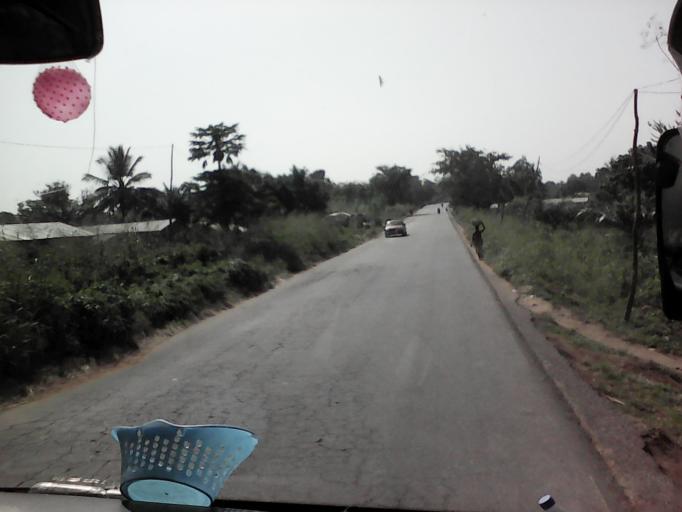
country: TG
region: Centrale
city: Sokode
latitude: 8.8362
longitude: 1.0768
